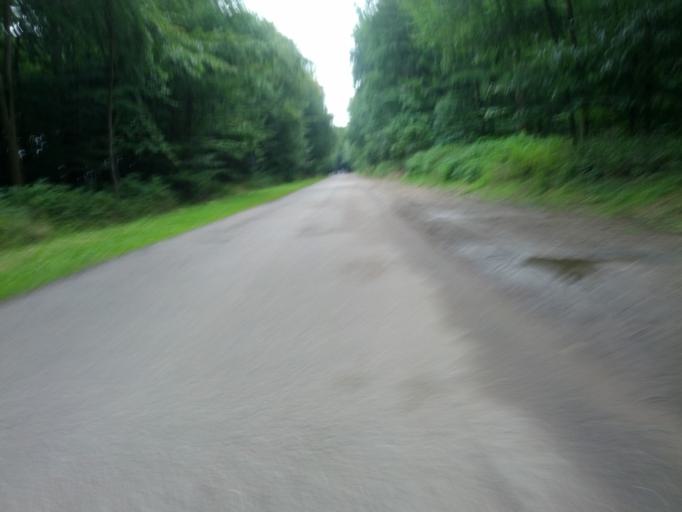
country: DE
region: Mecklenburg-Vorpommern
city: Ostseebad Kuhlungsborn
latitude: 54.1440
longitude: 11.8270
